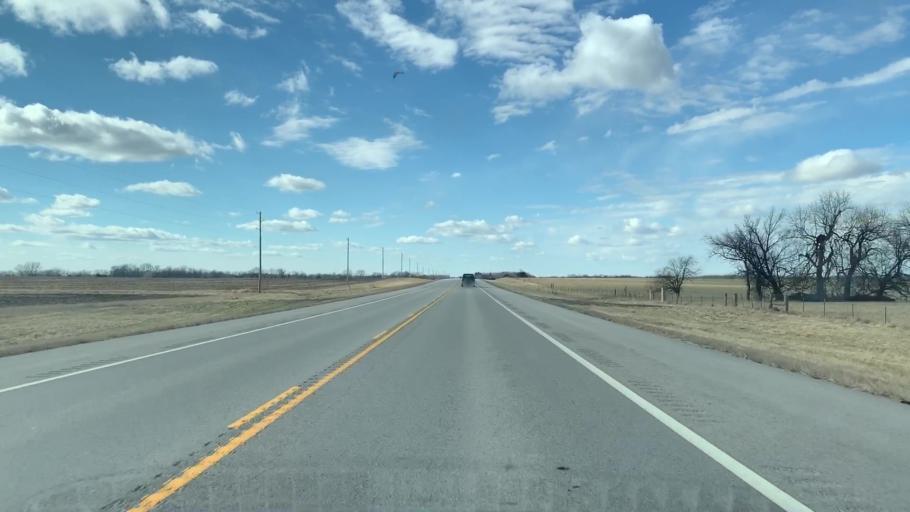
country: US
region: Kansas
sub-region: Labette County
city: Oswego
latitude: 37.3401
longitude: -95.0441
